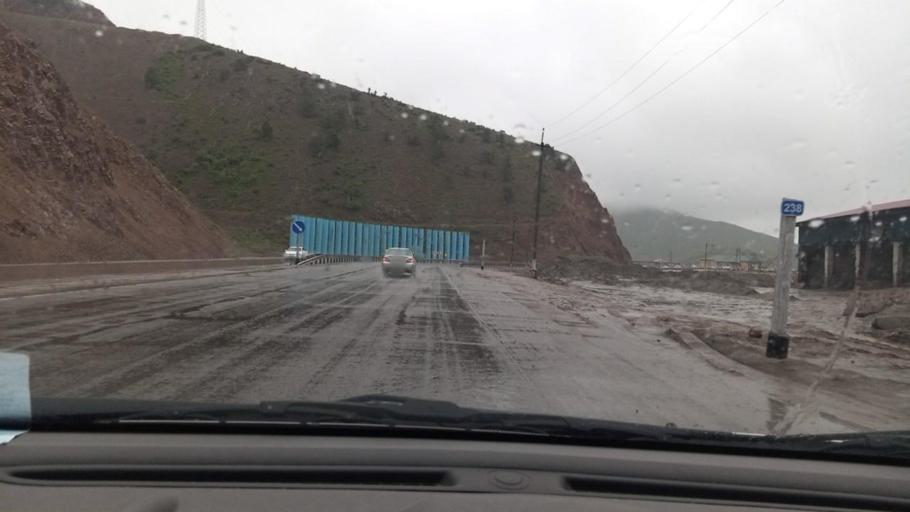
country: UZ
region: Toshkent
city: Angren
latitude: 41.0937
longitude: 70.5306
